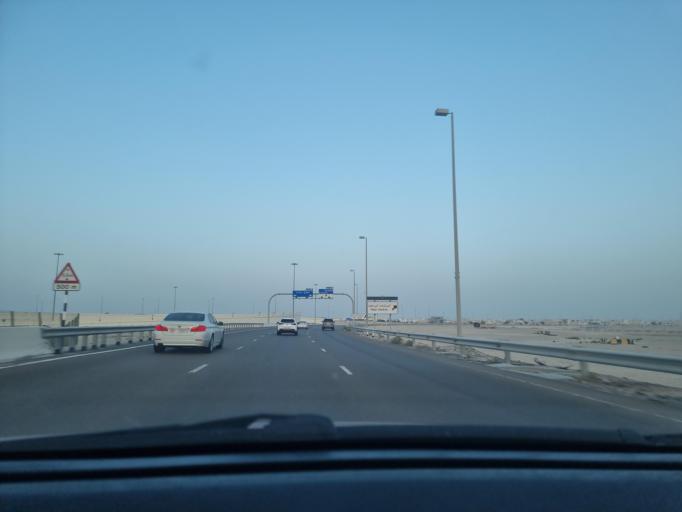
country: AE
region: Abu Dhabi
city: Abu Dhabi
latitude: 24.4132
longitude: 54.7104
